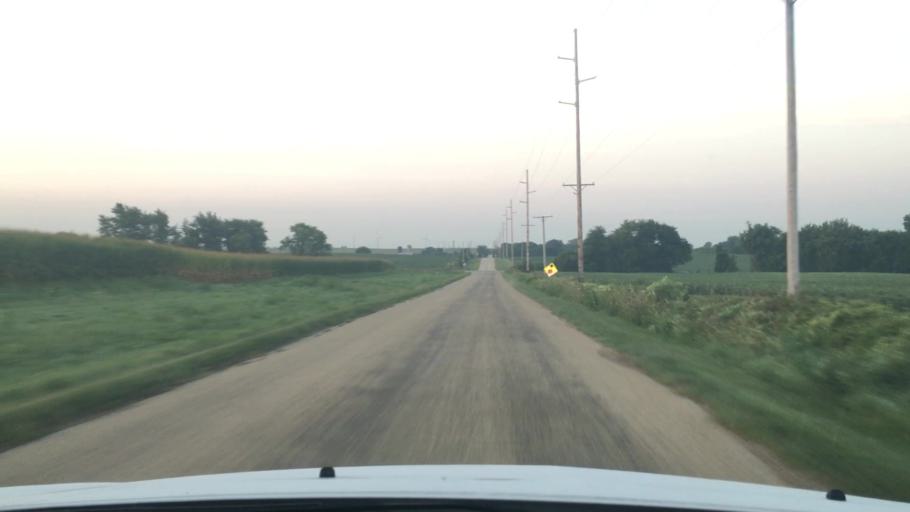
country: US
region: Illinois
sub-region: Ogle County
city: Rochelle
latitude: 41.8498
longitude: -89.0005
